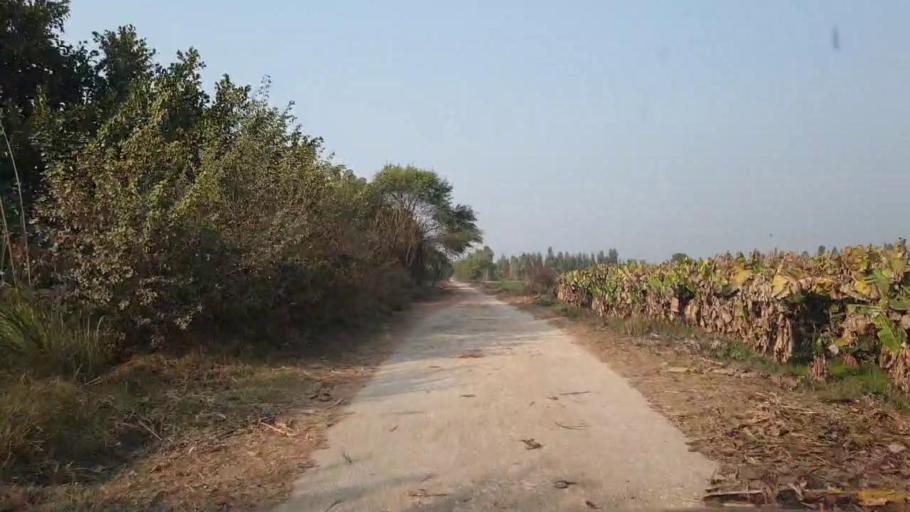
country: PK
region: Sindh
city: Hala
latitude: 25.9083
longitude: 68.4618
